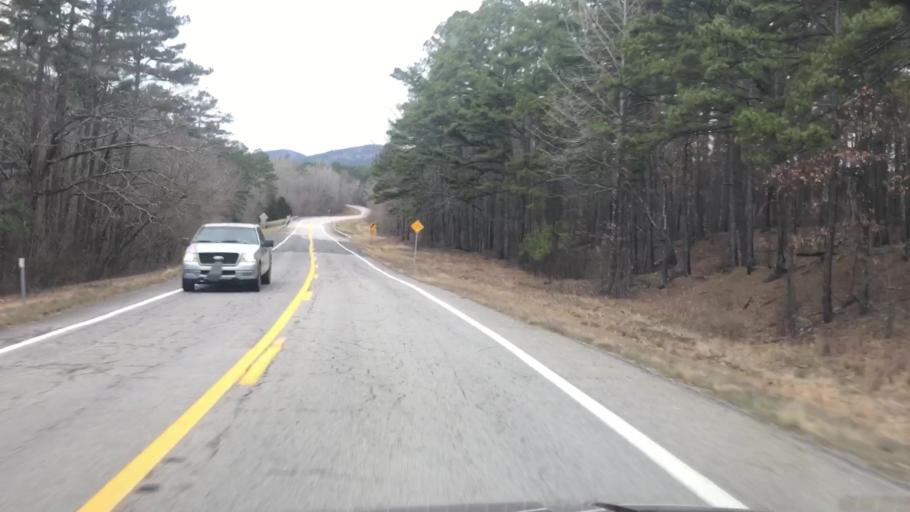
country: US
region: Arkansas
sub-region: Montgomery County
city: Mount Ida
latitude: 34.6846
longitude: -93.8029
